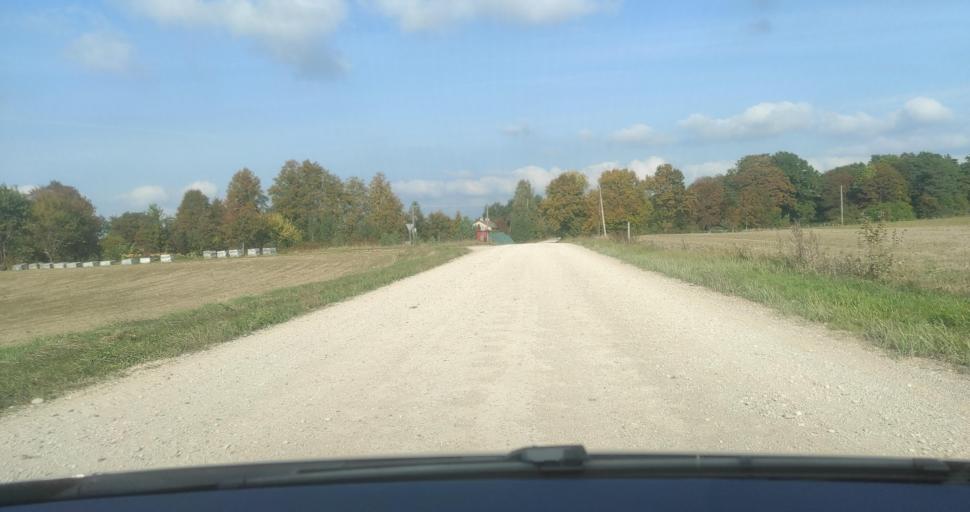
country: LV
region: Alsunga
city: Alsunga
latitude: 56.9958
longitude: 21.5836
